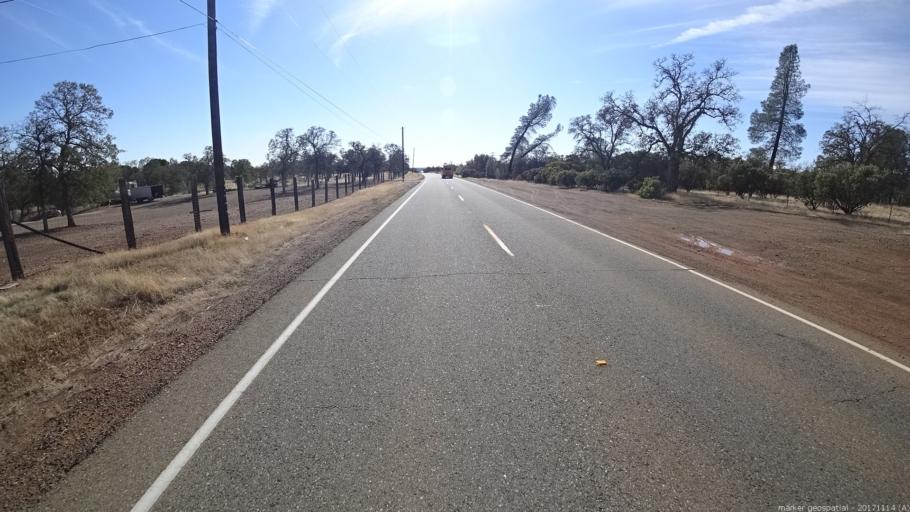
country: US
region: California
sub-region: Shasta County
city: Anderson
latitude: 40.4147
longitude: -122.4068
